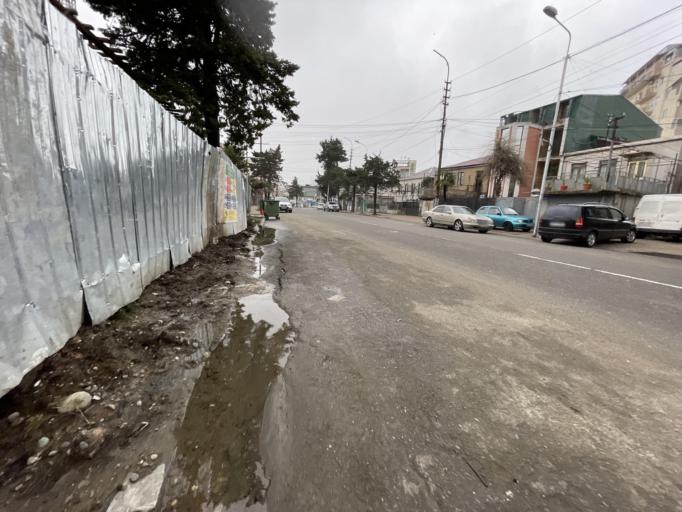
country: GE
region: Ajaria
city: Batumi
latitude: 41.6367
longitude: 41.6443
